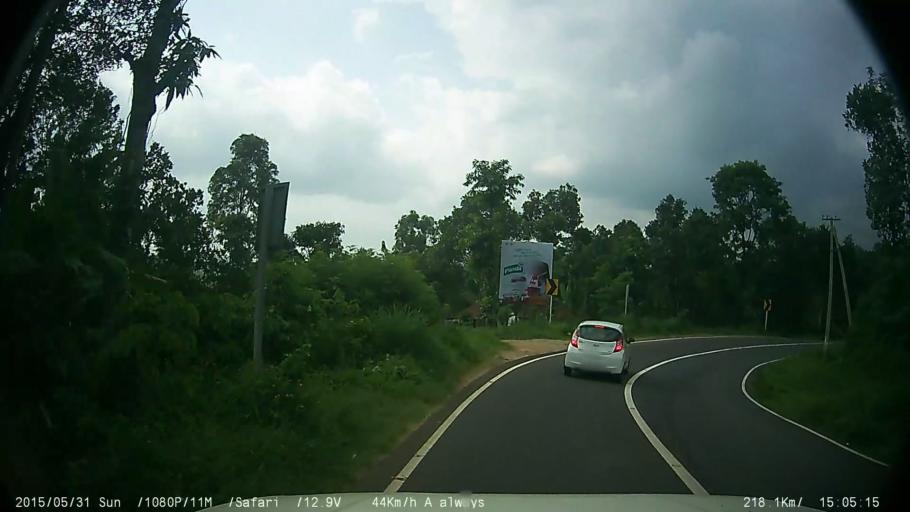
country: IN
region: Kerala
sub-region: Wayanad
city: Kalpetta
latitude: 11.6381
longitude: 76.2131
